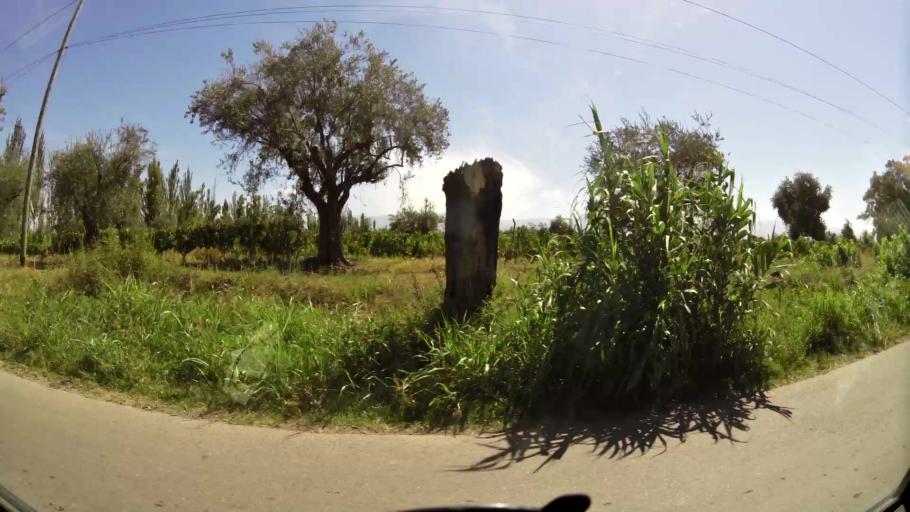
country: AR
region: Mendoza
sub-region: Departamento de Godoy Cruz
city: Godoy Cruz
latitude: -32.9850
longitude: -68.8436
